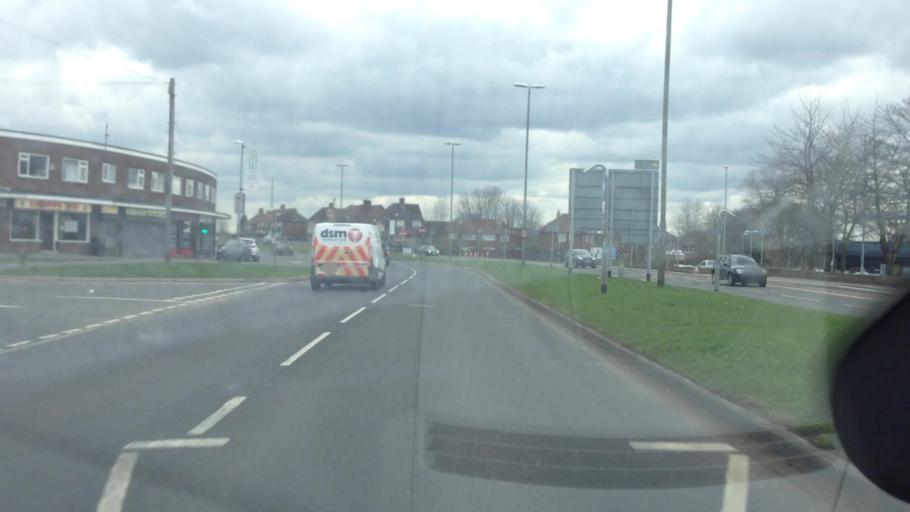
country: GB
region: England
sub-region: City and Borough of Leeds
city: Scholes
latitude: 53.8147
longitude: -1.4543
